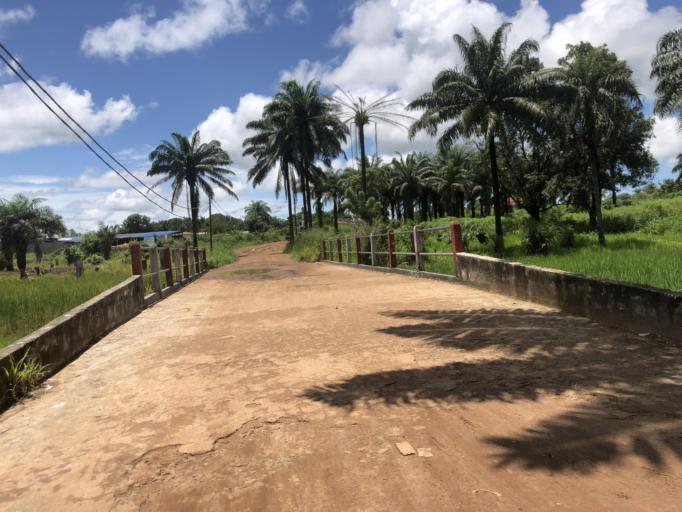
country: SL
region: Northern Province
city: Makeni
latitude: 8.8483
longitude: -12.0567
